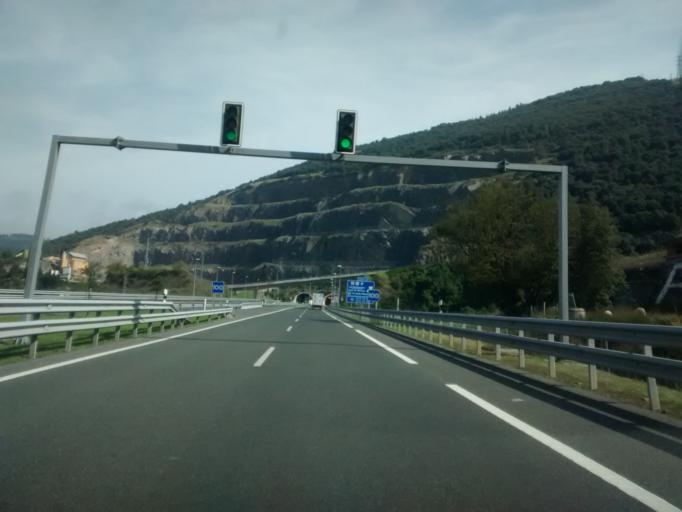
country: ES
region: Basque Country
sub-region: Provincia de Guipuzcoa
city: Arrasate / Mondragon
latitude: 43.0526
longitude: -2.4914
